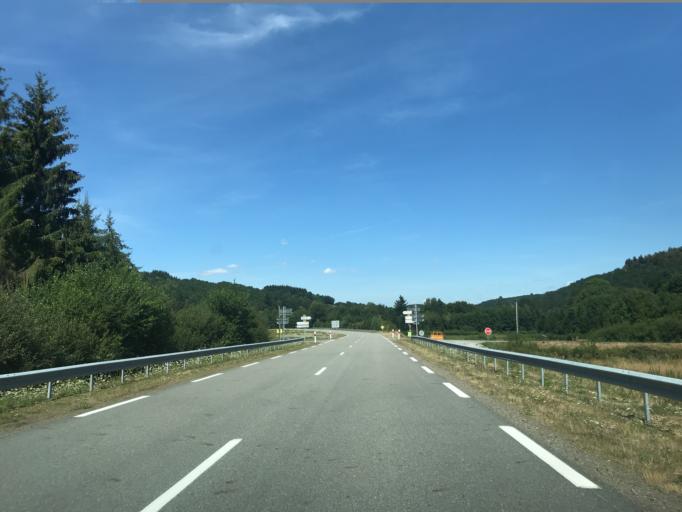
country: FR
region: Limousin
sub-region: Departement de la Creuse
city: Felletin
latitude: 45.8165
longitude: 2.1622
